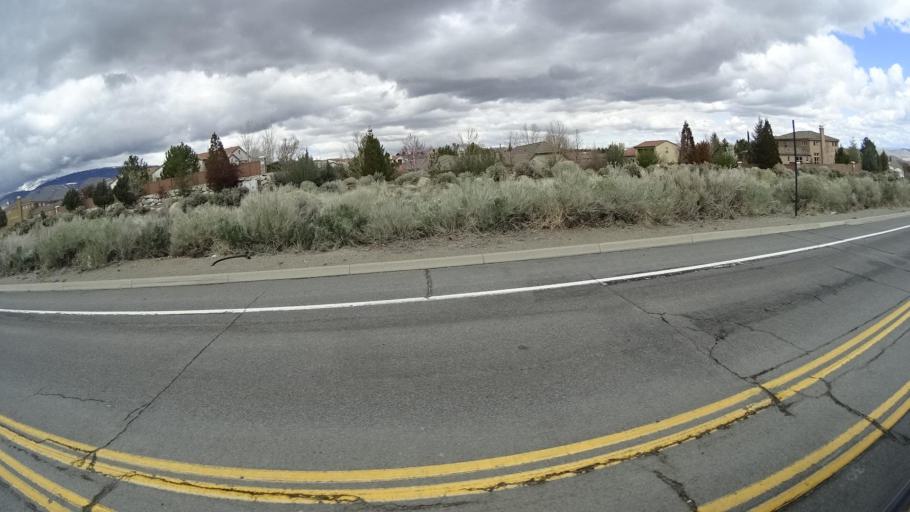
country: US
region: Nevada
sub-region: Washoe County
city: Sparks
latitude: 39.4071
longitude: -119.7629
